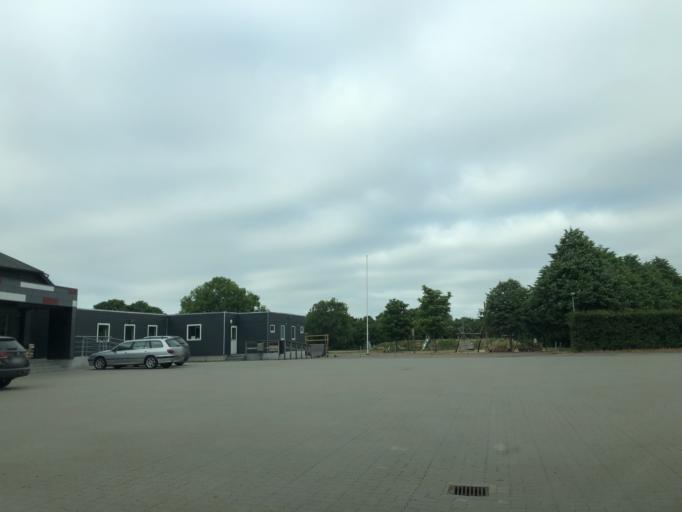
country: DK
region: Central Jutland
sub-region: Holstebro Kommune
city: Vinderup
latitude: 56.3905
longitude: 8.7987
